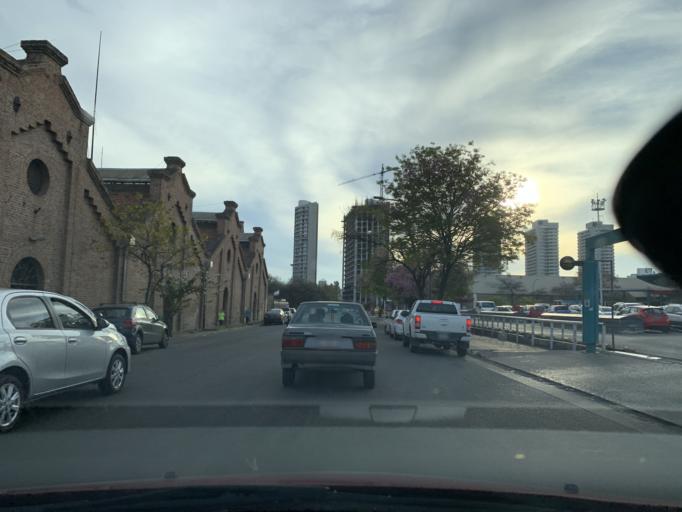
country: AR
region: Cordoba
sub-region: Departamento de Capital
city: Cordoba
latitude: -31.4088
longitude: -64.1693
